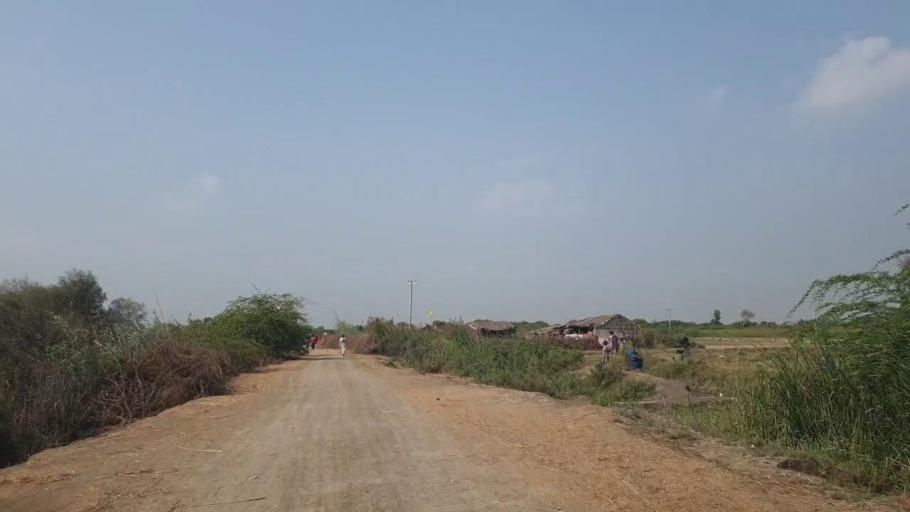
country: PK
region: Sindh
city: Badin
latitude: 24.7498
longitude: 68.7556
